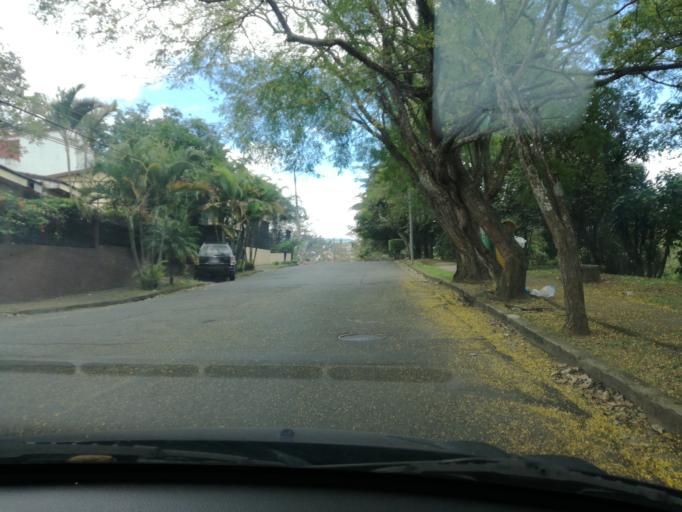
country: CR
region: San Jose
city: Curridabat
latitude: 9.9085
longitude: -84.0336
